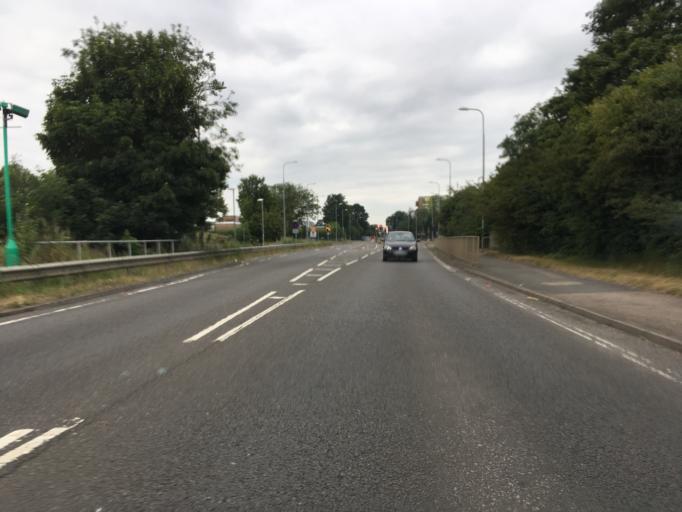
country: GB
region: England
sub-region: Central Bedfordshire
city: Kensworth
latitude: 51.8726
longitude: -0.5001
